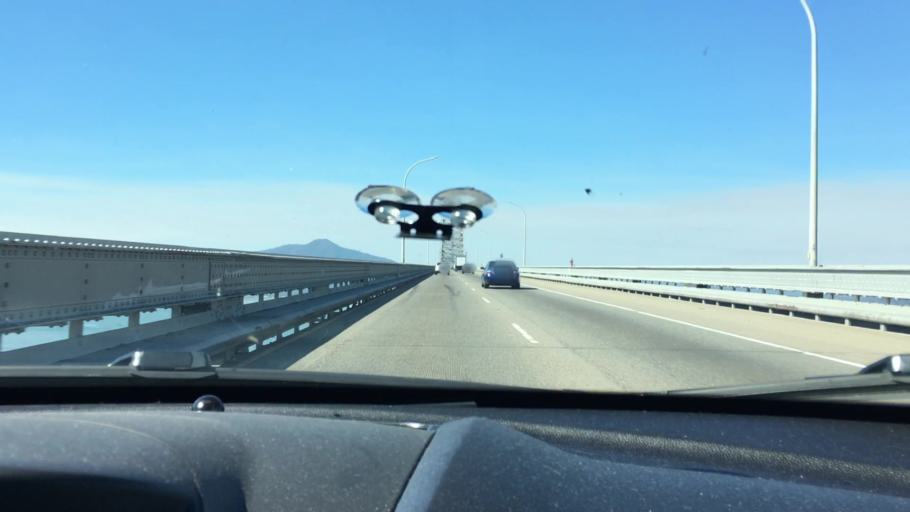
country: US
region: California
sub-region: Marin County
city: Tiburon
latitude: 37.9345
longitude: -122.4361
